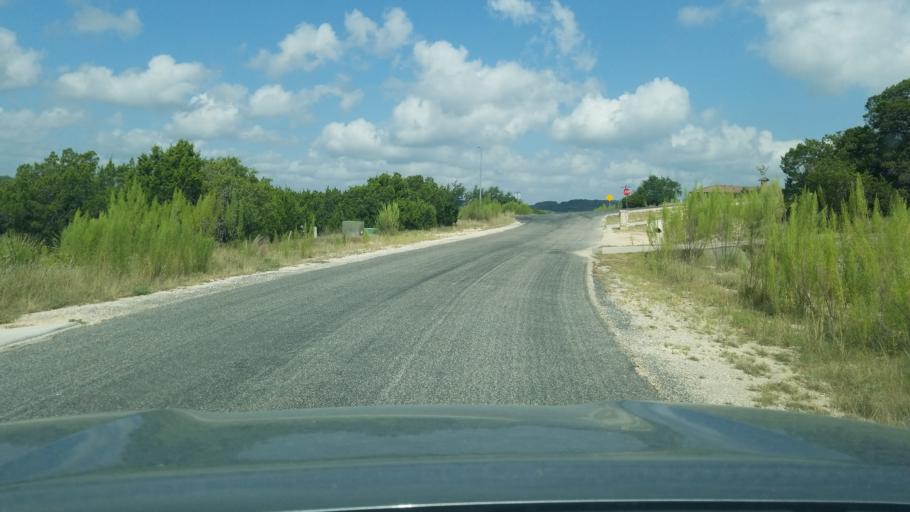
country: US
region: Texas
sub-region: Bexar County
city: Timberwood Park
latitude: 29.6838
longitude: -98.5191
